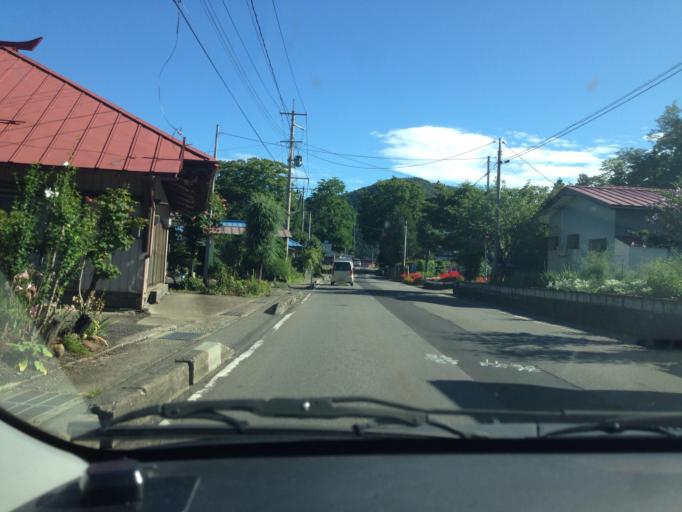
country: JP
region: Fukushima
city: Inawashiro
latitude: 37.3928
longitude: 140.1296
